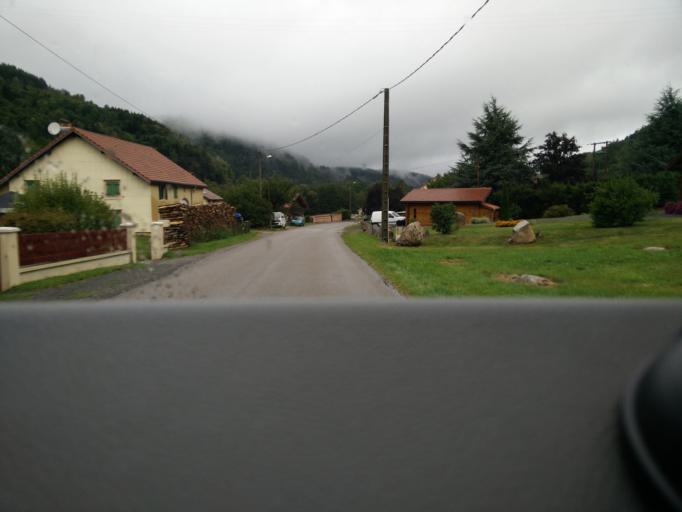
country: FR
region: Lorraine
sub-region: Departement des Vosges
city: Plainfaing
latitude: 48.1500
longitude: 7.0089
